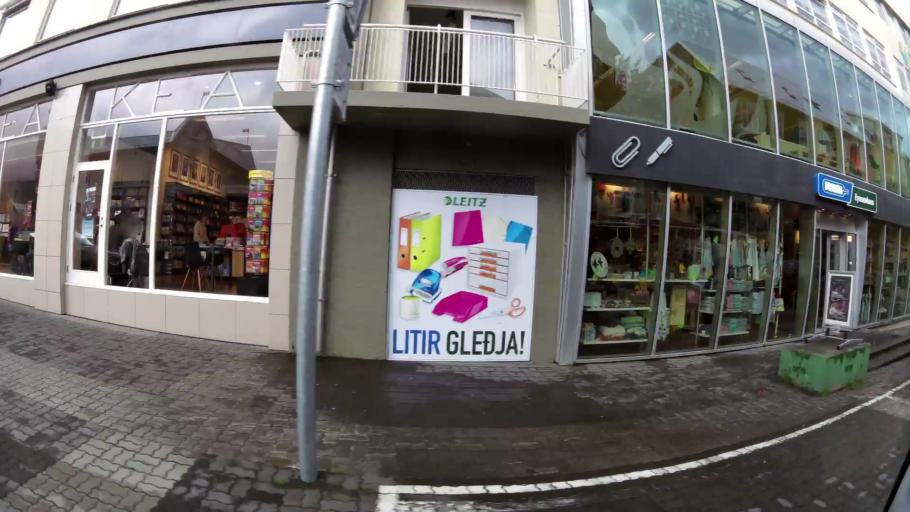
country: IS
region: Northeast
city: Akureyri
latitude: 65.6811
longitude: -18.0901
